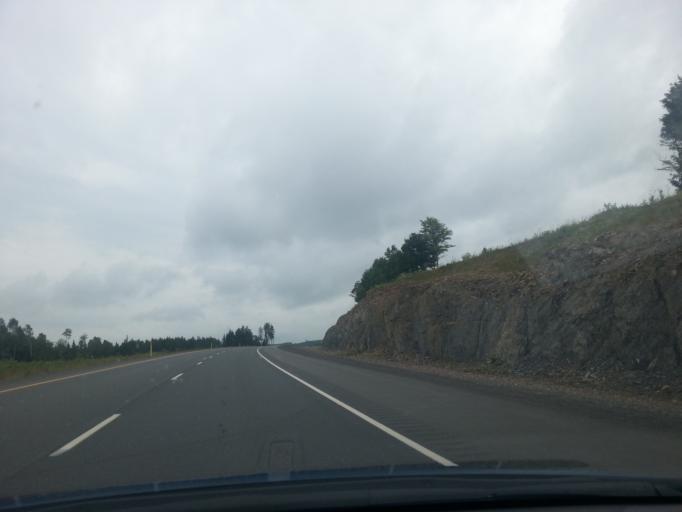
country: US
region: Maine
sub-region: Aroostook County
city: Easton
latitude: 46.5876
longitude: -67.7421
